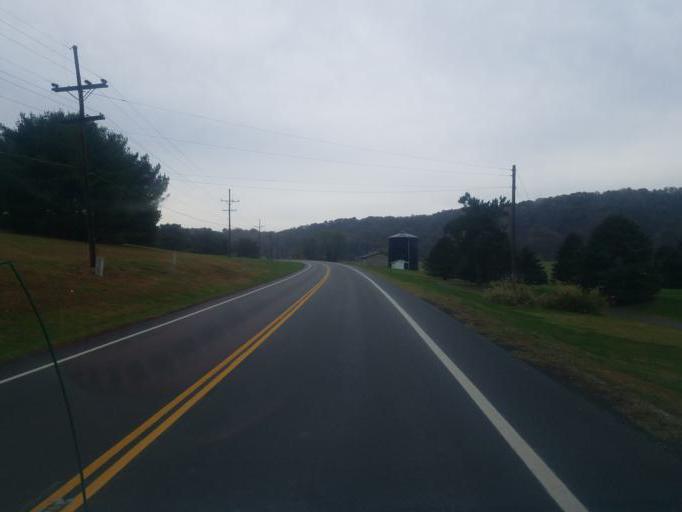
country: US
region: Ohio
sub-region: Washington County
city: Beverly
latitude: 39.5486
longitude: -81.5935
